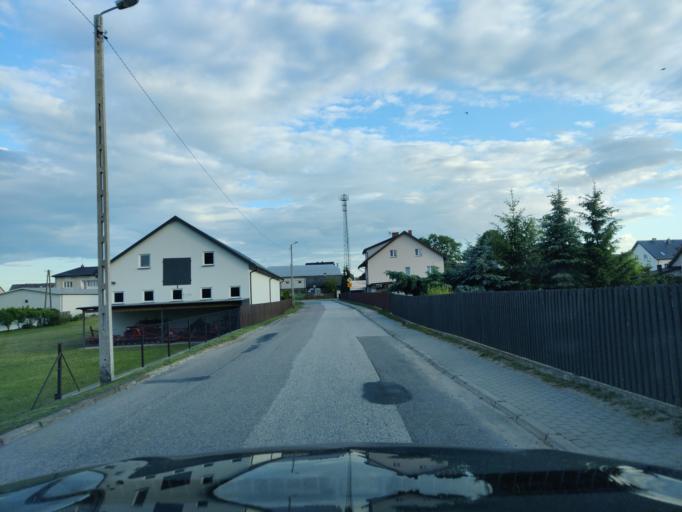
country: PL
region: Masovian Voivodeship
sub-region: Powiat pultuski
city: Obryte
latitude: 52.7567
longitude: 21.2168
